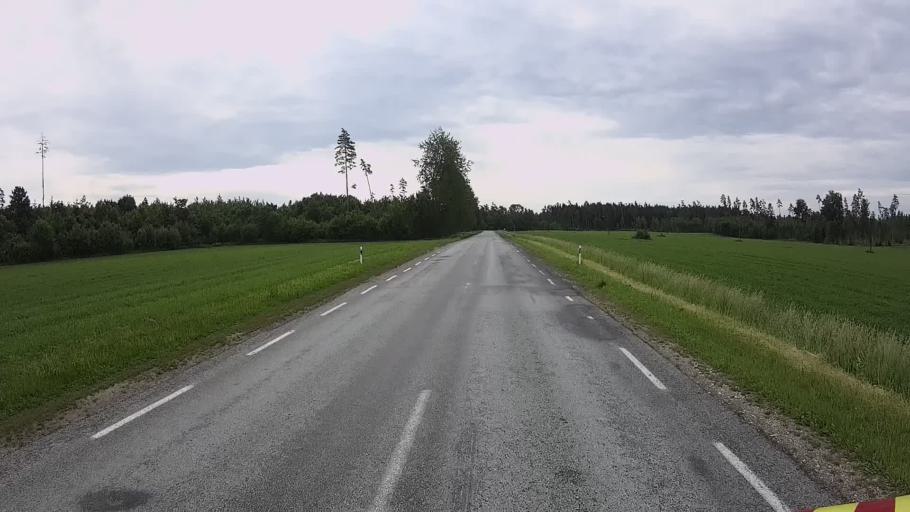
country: EE
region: Viljandimaa
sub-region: Karksi vald
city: Karksi-Nuia
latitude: 58.2271
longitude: 25.6080
